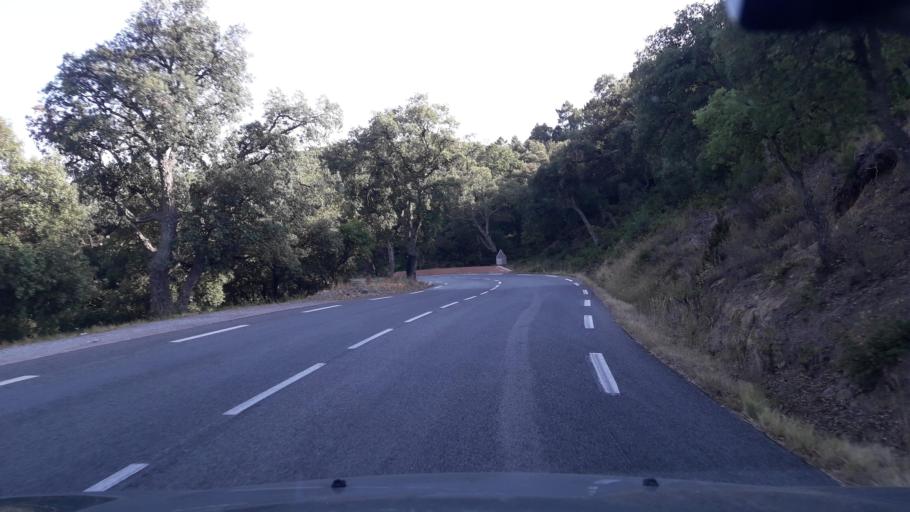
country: FR
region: Provence-Alpes-Cote d'Azur
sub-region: Departement du Var
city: Saint-Raphael
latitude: 43.4863
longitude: 6.7761
